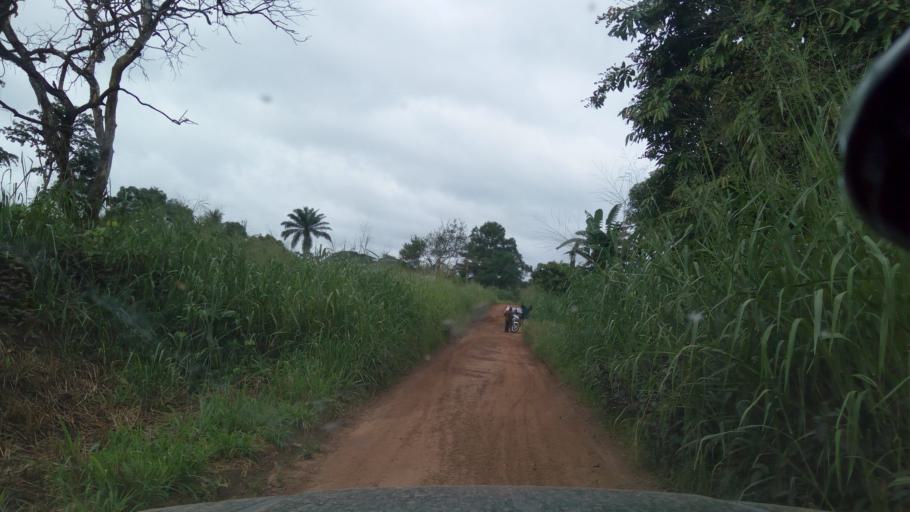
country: SL
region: Eastern Province
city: Kenema
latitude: 7.7597
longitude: -11.1891
